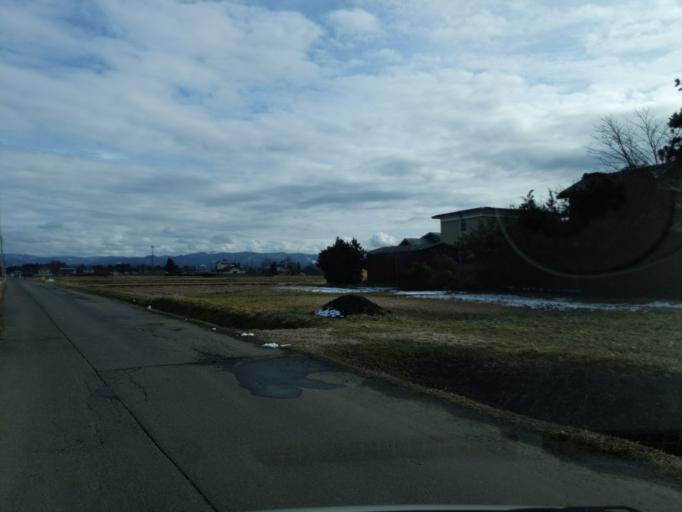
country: JP
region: Iwate
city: Mizusawa
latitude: 39.1715
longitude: 141.1300
